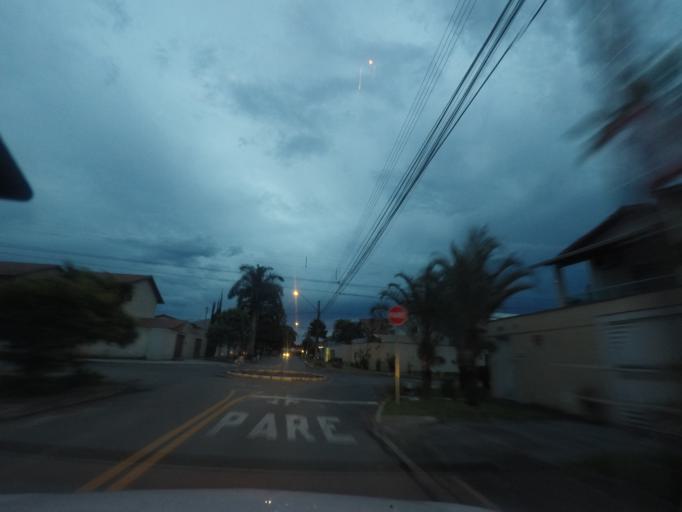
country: BR
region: Goias
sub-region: Goiania
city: Goiania
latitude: -16.7186
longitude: -49.3042
